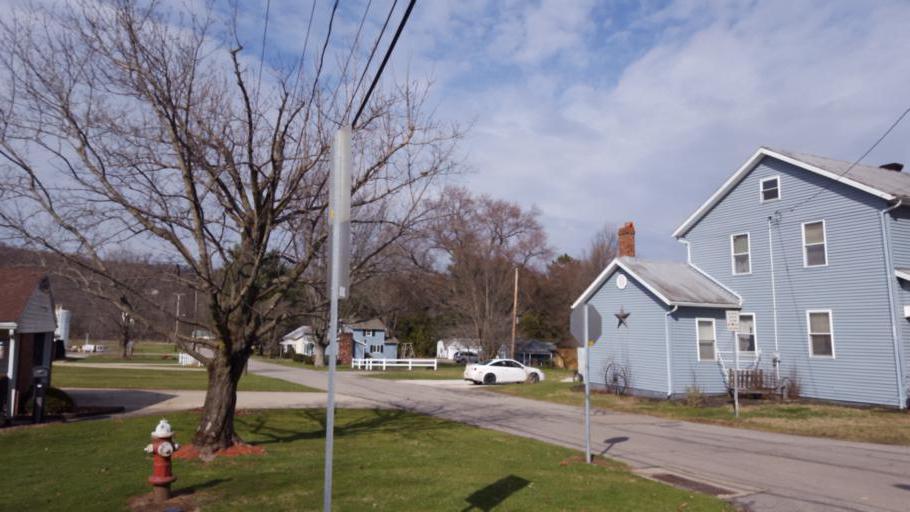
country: US
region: Ohio
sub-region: Sandusky County
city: Bellville
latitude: 40.6222
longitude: -82.5152
